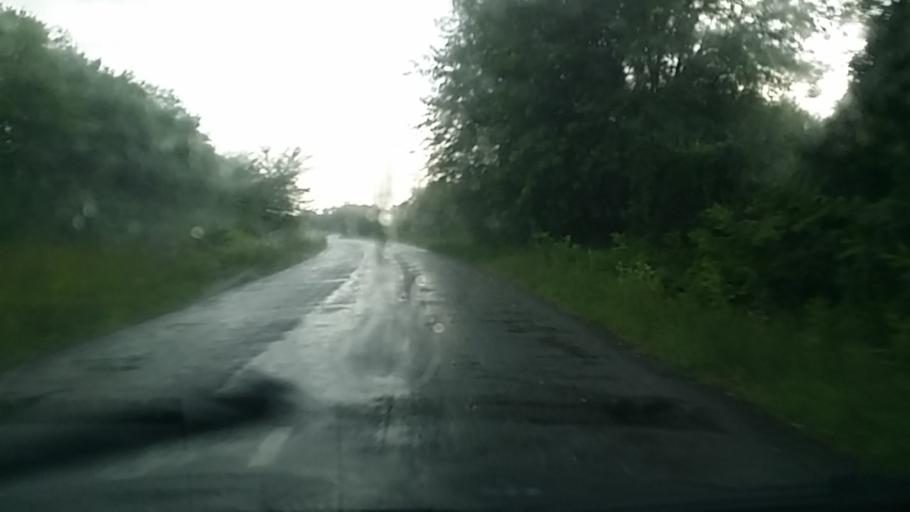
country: HU
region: Pest
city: Ocsa
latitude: 47.2895
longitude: 19.2592
